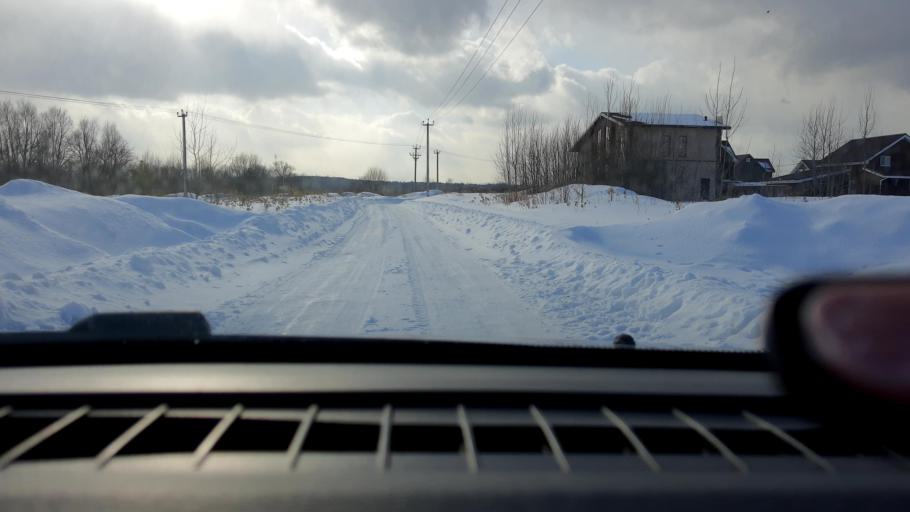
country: RU
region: Nizjnij Novgorod
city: Lukino
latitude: 56.4196
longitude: 43.7197
